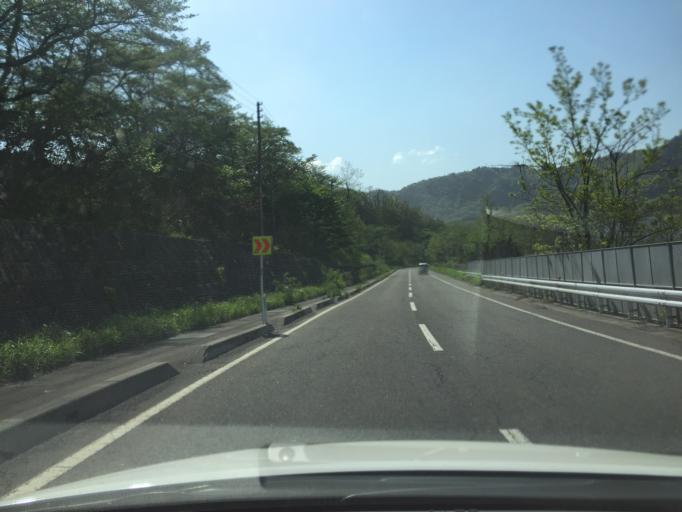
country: JP
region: Niigata
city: Shibata
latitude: 37.7018
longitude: 139.4838
